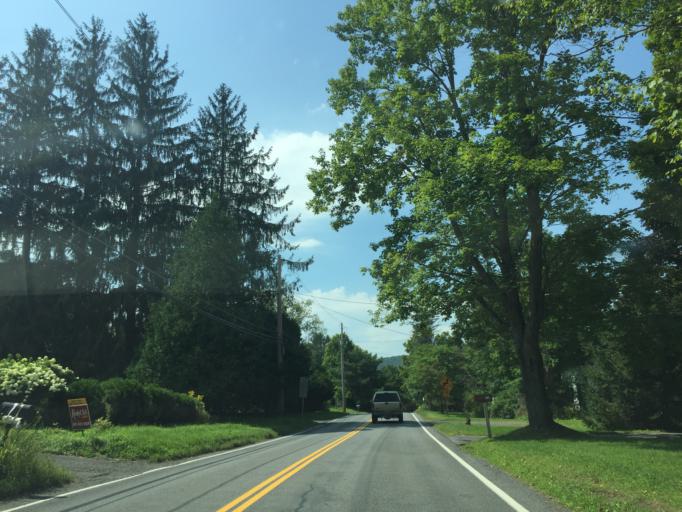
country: US
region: New York
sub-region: Otsego County
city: Cooperstown
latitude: 42.6858
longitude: -74.9145
